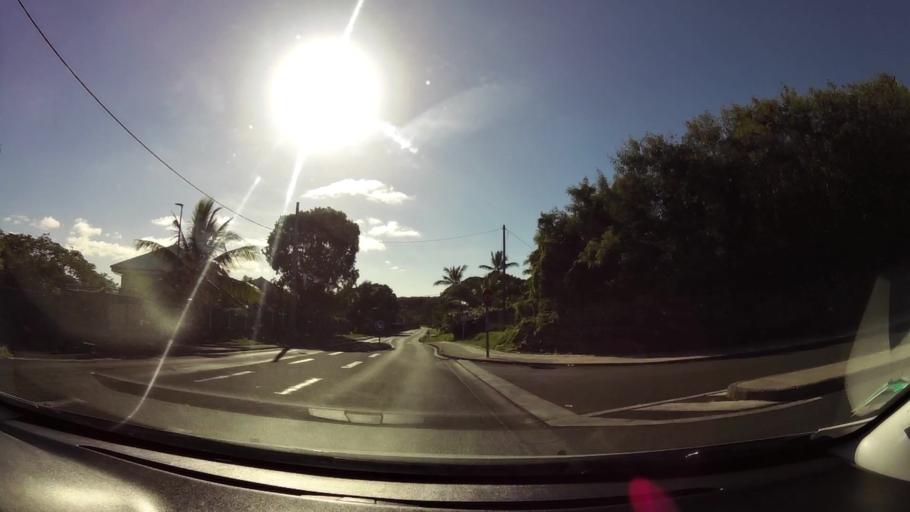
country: YT
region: Pamandzi
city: Pamandzi
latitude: -12.7949
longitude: 45.2729
